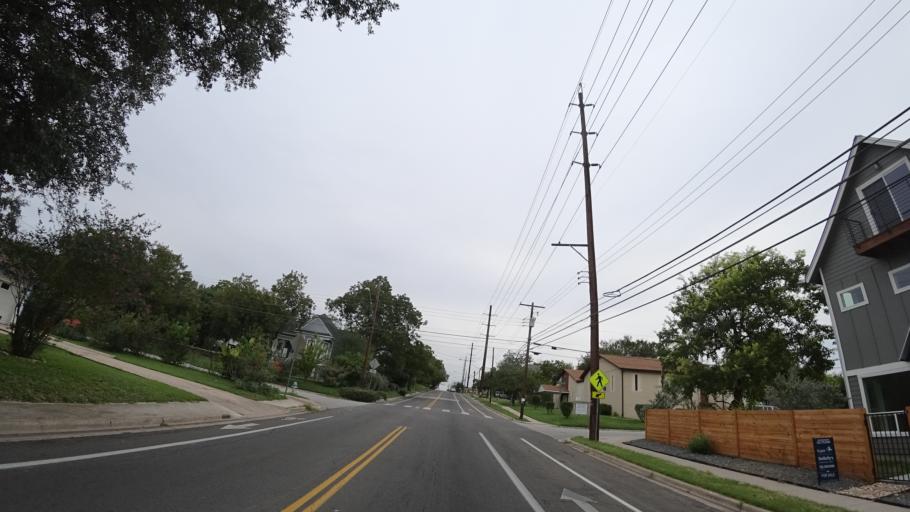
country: US
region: Texas
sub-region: Travis County
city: Austin
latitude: 30.2781
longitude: -97.7168
